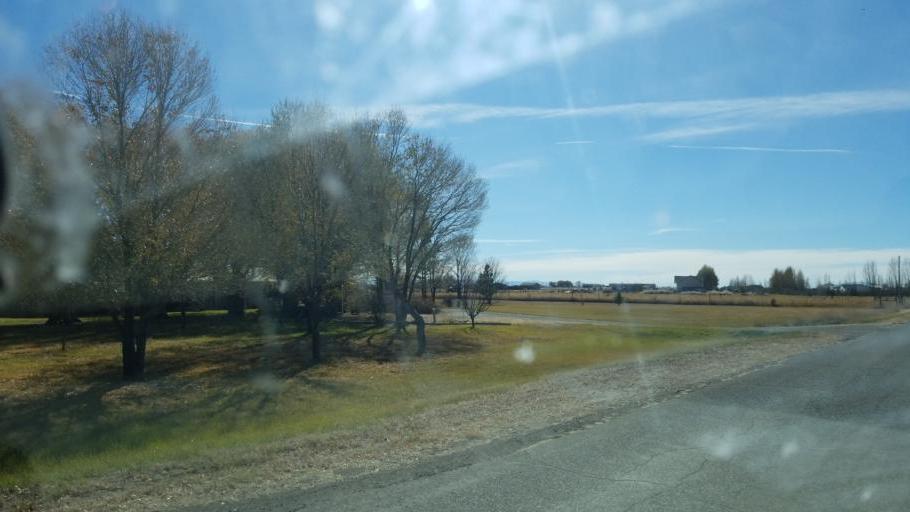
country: US
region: Colorado
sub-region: Rio Grande County
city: Monte Vista
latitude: 37.5604
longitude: -106.1306
